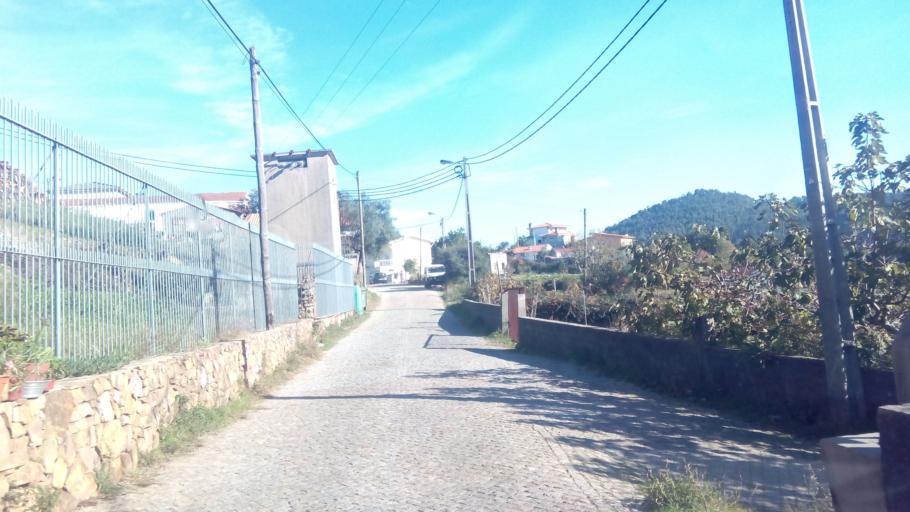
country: PT
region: Porto
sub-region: Paredes
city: Gandra
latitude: 41.1902
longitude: -8.4111
